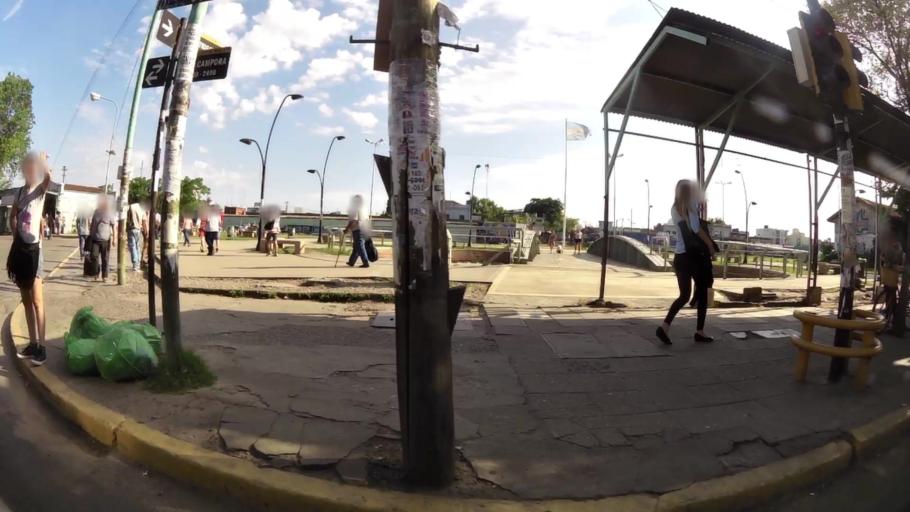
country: AR
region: Buenos Aires
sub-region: Partido de Merlo
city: Merlo
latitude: -34.6636
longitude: -58.7275
